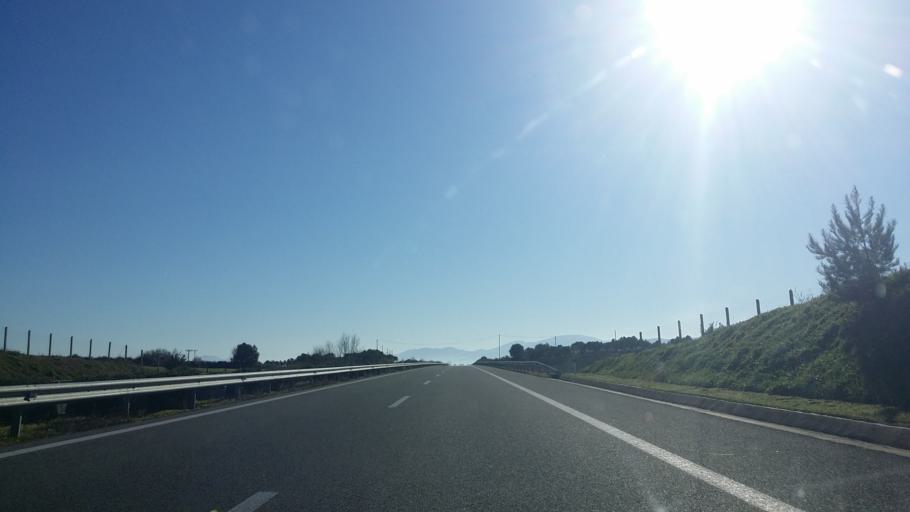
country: GR
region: West Greece
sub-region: Nomos Aitolias kai Akarnanias
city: Fitiai
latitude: 38.6715
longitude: 21.2281
